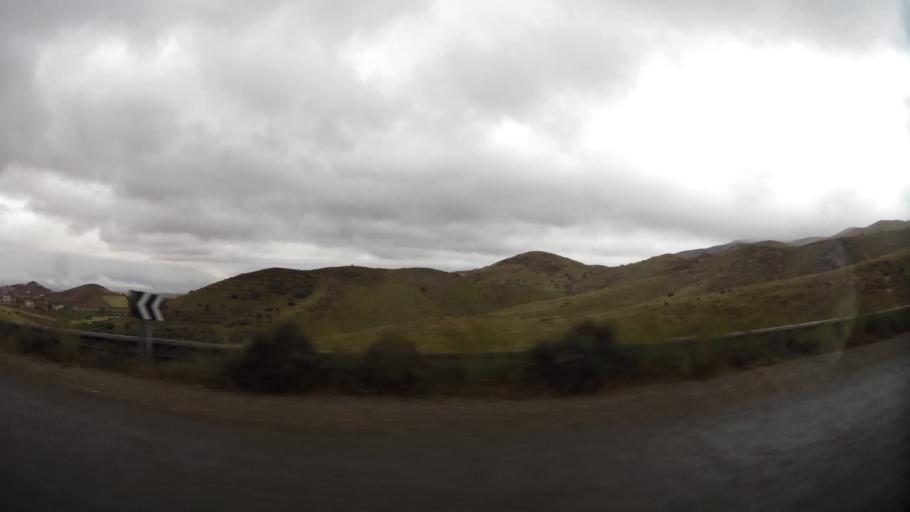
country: MA
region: Oriental
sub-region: Nador
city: Midar
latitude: 35.0660
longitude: -3.4796
